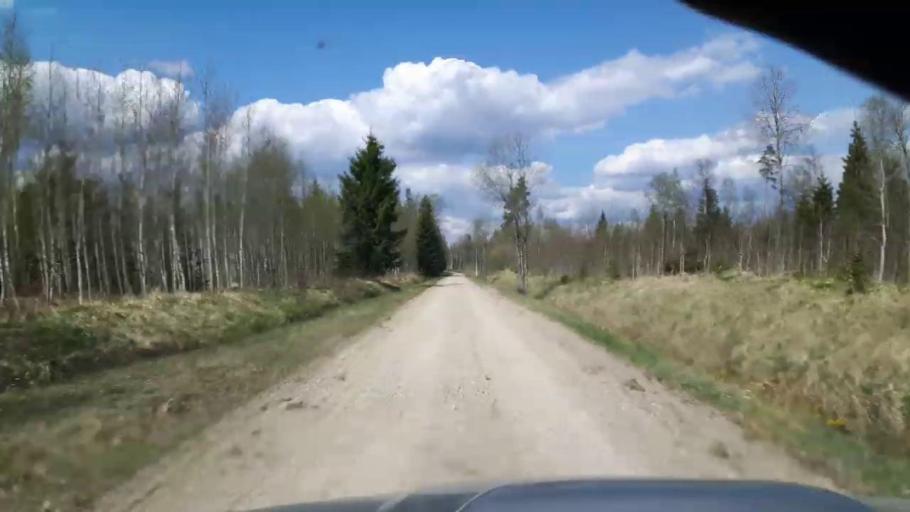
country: EE
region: Paernumaa
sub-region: Tootsi vald
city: Tootsi
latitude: 58.4504
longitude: 24.8985
